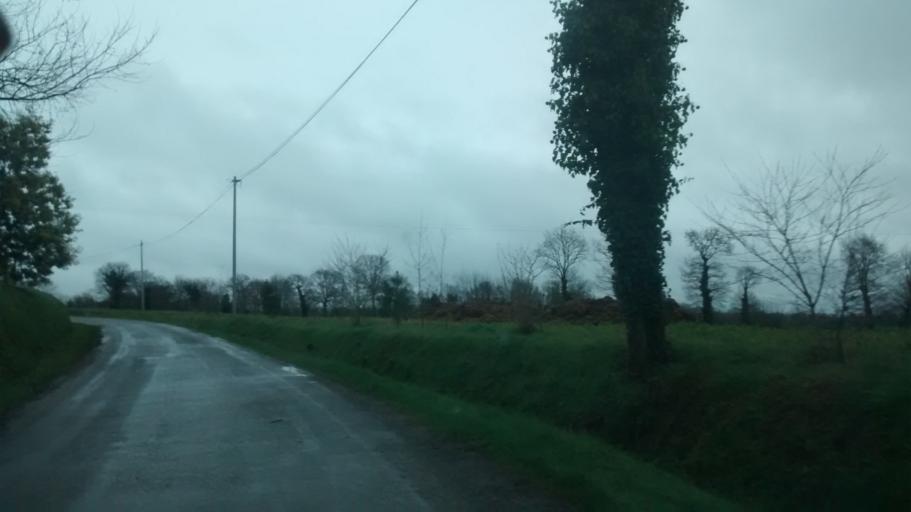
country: FR
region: Brittany
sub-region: Departement d'Ille-et-Vilaine
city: Melesse
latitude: 48.2061
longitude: -1.6710
